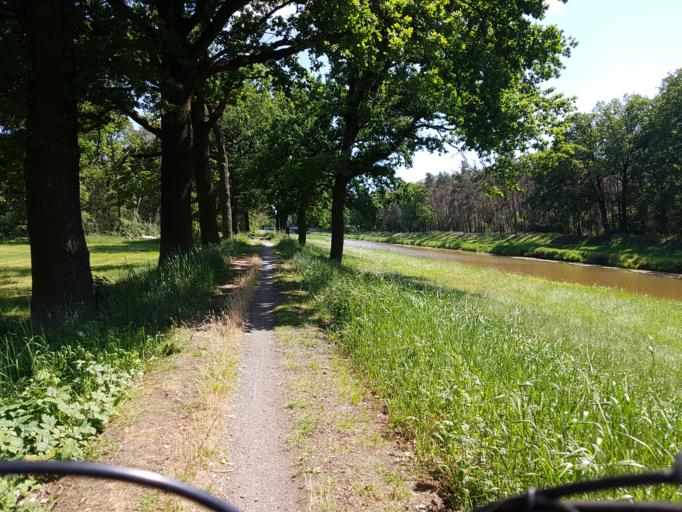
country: DE
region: Brandenburg
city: Bad Liebenwerda
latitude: 51.4889
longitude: 13.4308
